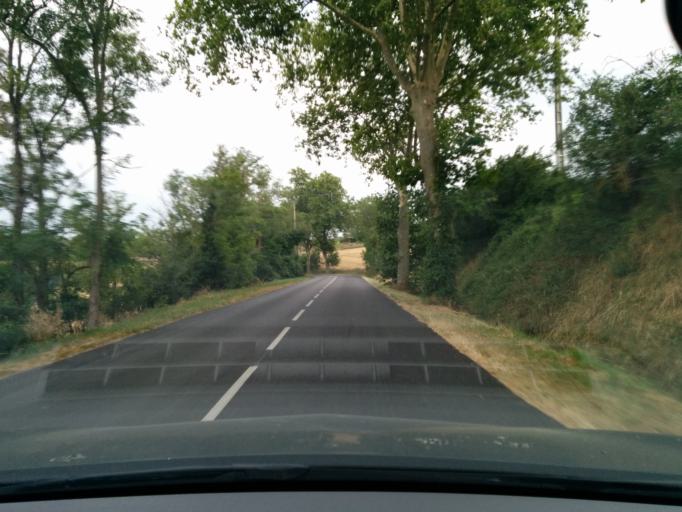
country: FR
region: Midi-Pyrenees
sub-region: Departement de la Haute-Garonne
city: Venerque
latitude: 43.4770
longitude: 1.4547
